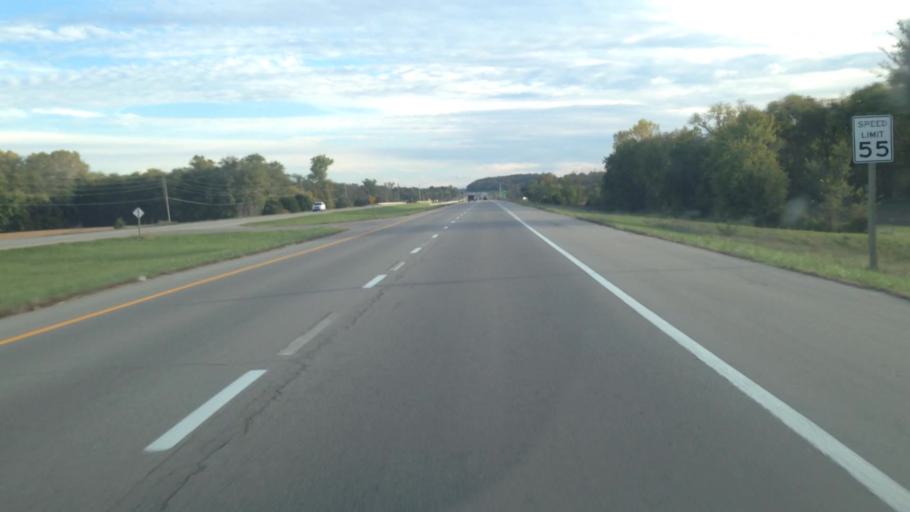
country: US
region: Kansas
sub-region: Douglas County
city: Lawrence
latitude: 38.9142
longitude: -95.2608
